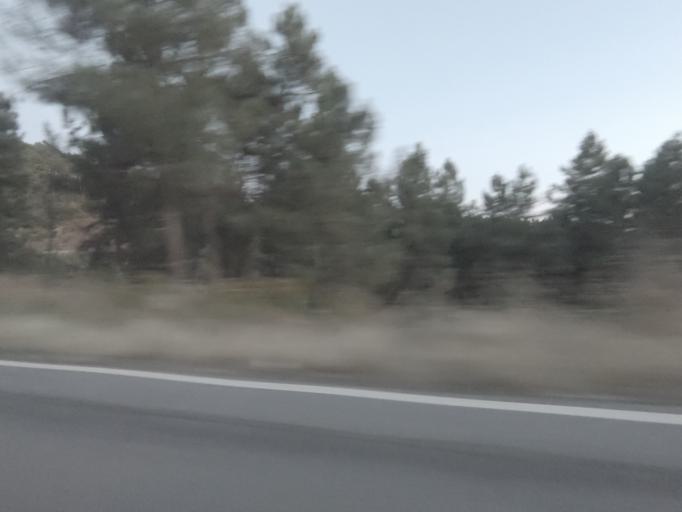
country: PT
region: Vila Real
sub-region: Sabrosa
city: Vilela
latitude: 41.2307
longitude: -7.6784
